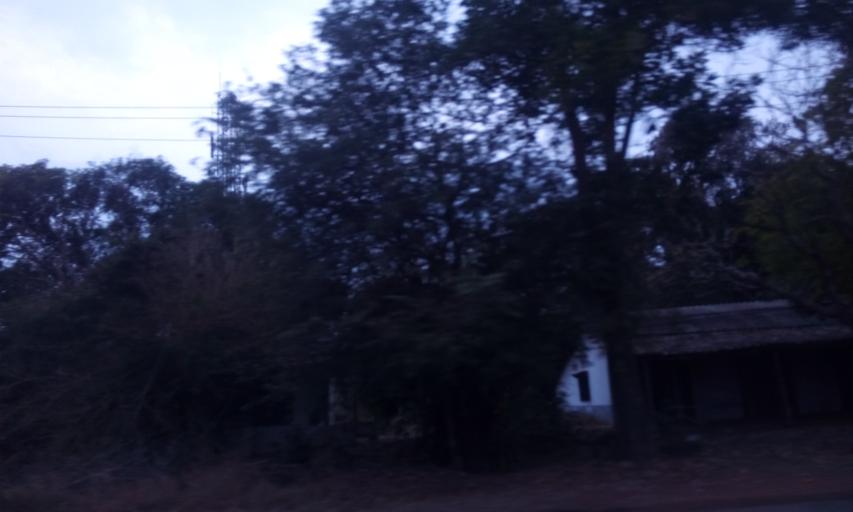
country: TH
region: Chanthaburi
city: Khlung
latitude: 12.4235
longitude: 102.3210
